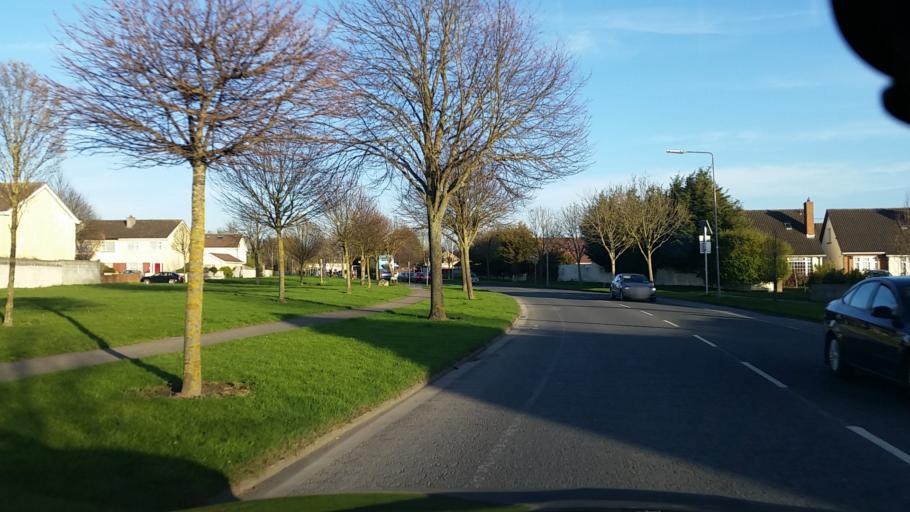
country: IE
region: Leinster
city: Hartstown
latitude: 53.3915
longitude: -6.4175
